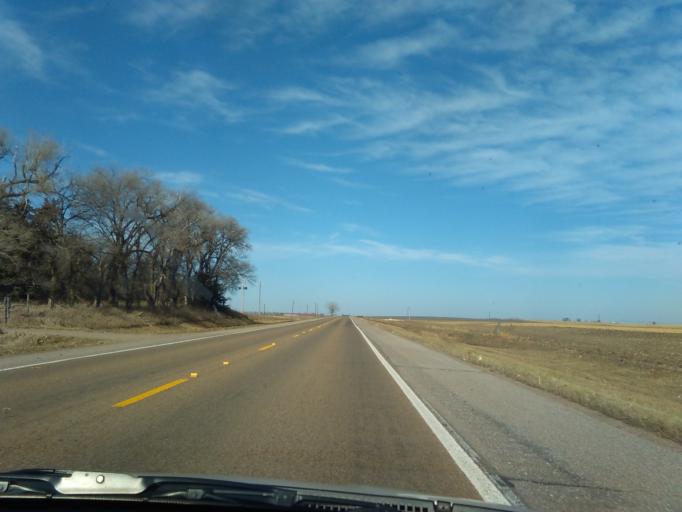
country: US
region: Nebraska
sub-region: Clay County
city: Clay Center
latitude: 40.5498
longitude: -98.0514
